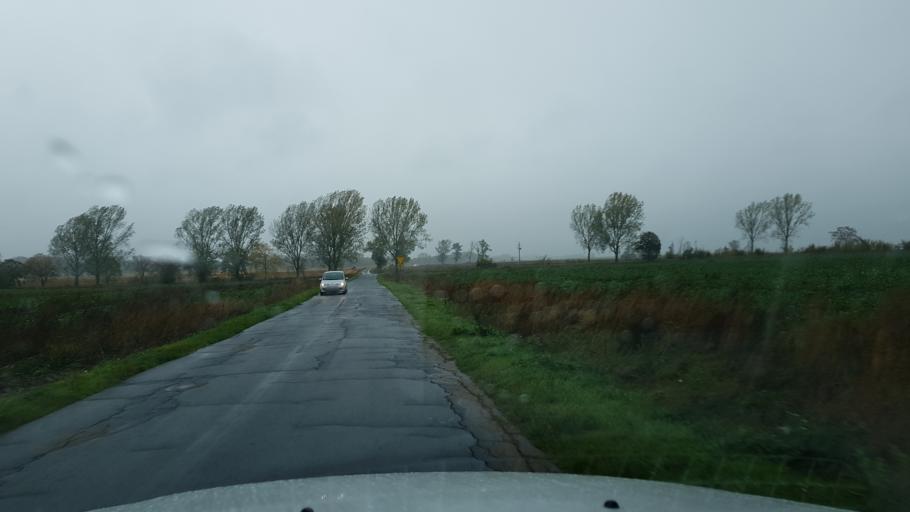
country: PL
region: West Pomeranian Voivodeship
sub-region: Powiat pyrzycki
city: Kozielice
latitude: 53.1707
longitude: 14.8181
